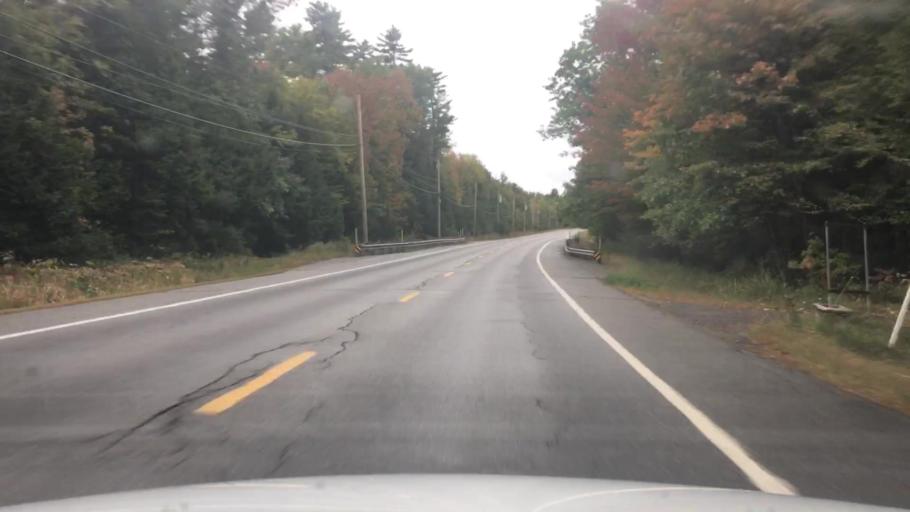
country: US
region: Maine
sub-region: Kennebec County
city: Rome
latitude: 44.5135
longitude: -69.8746
